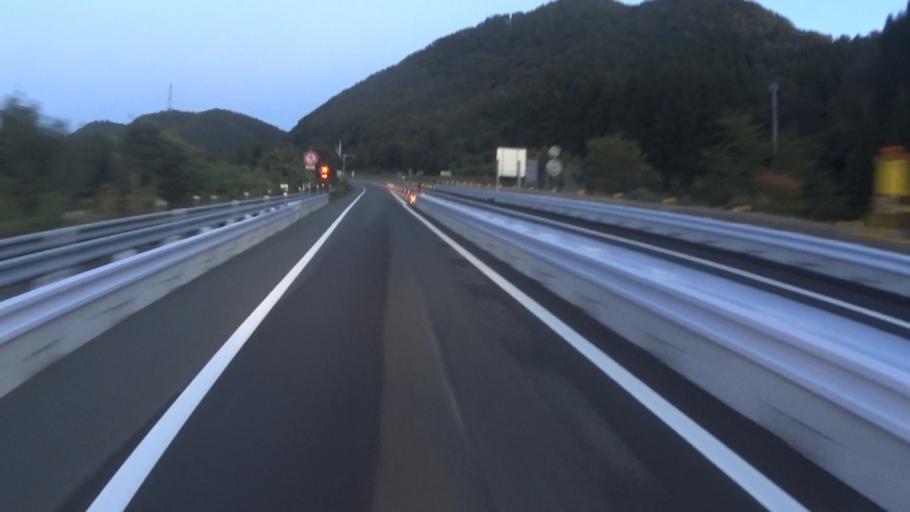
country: JP
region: Kyoto
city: Kameoka
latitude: 35.1454
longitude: 135.4344
